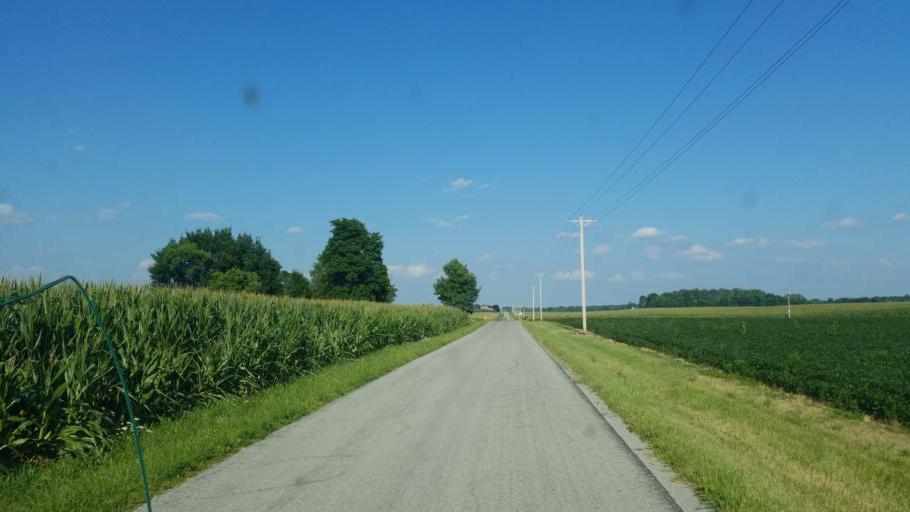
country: US
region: Ohio
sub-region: Wyandot County
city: Upper Sandusky
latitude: 40.7893
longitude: -83.1521
